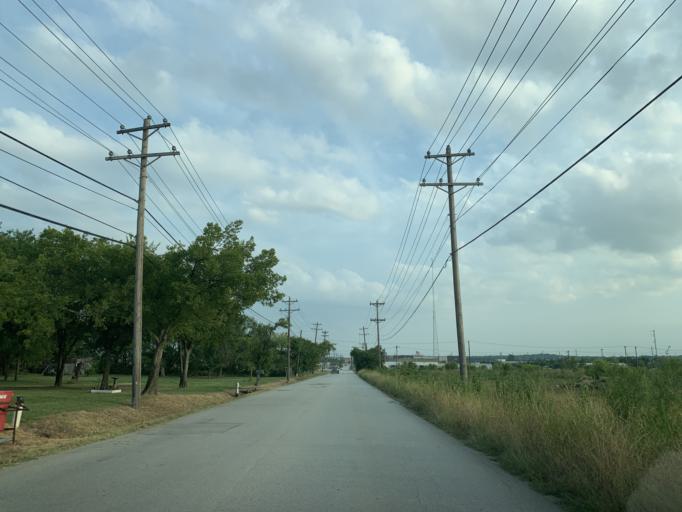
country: US
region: Texas
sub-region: Tarrant County
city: Keller
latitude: 32.9407
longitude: -97.2553
